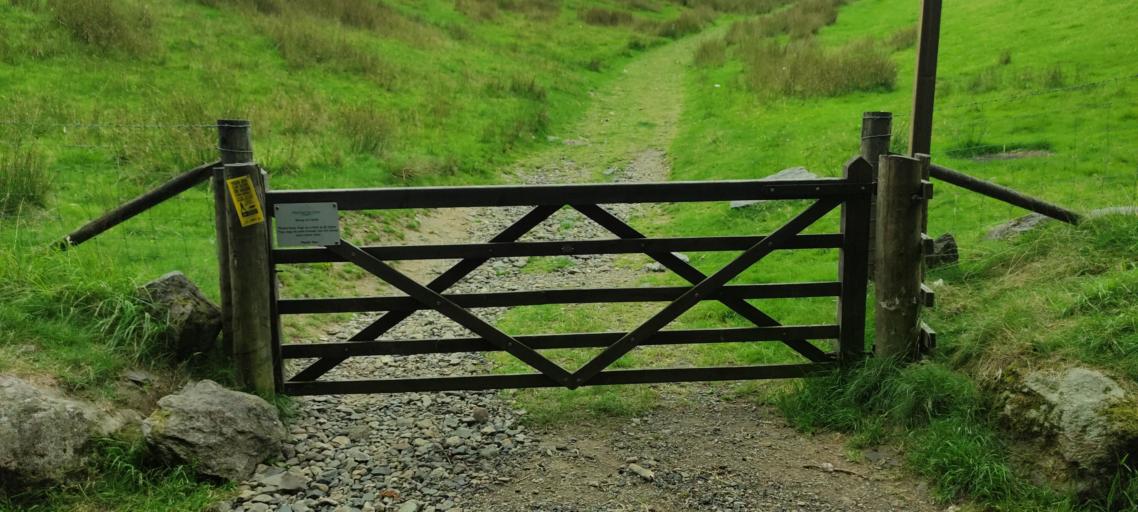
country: GB
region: England
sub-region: Cumbria
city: Ambleside
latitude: 54.5338
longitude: -2.9494
